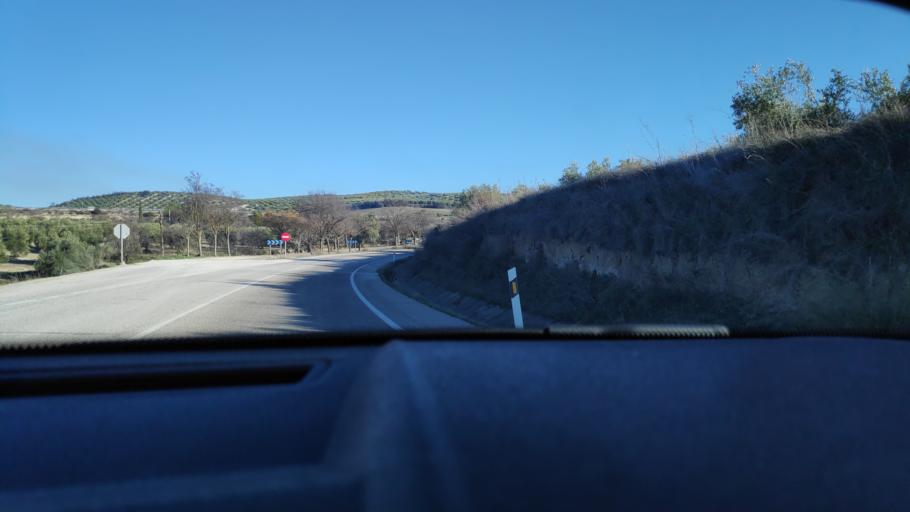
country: ES
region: Andalusia
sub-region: Province of Cordoba
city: Baena
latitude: 37.6005
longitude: -4.3083
